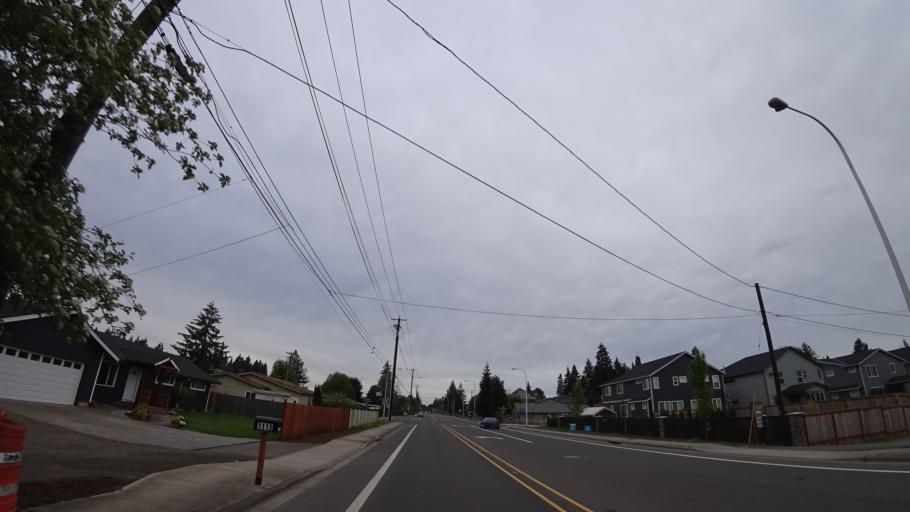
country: US
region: Oregon
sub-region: Washington County
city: Hillsboro
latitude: 45.5116
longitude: -122.9367
